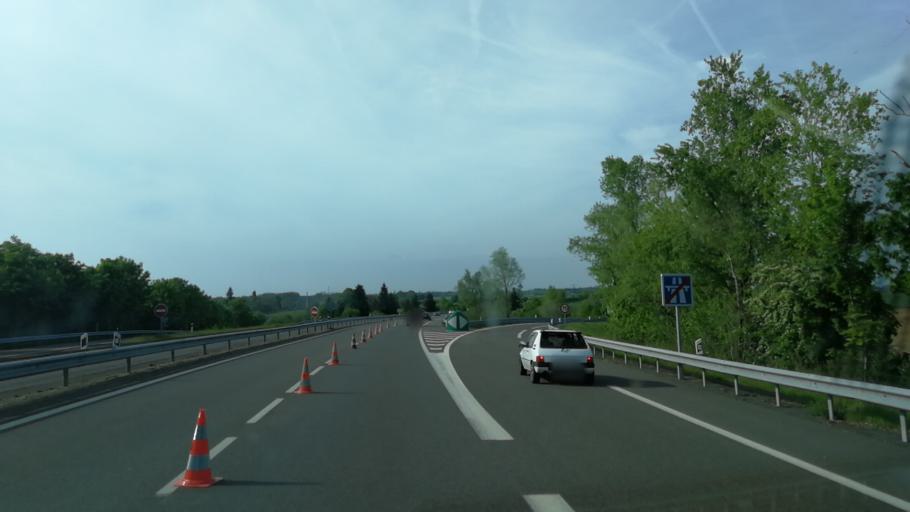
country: FR
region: Bourgogne
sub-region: Departement de la Nievre
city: La Charite-sur-Loire
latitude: 47.1325
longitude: 3.0442
